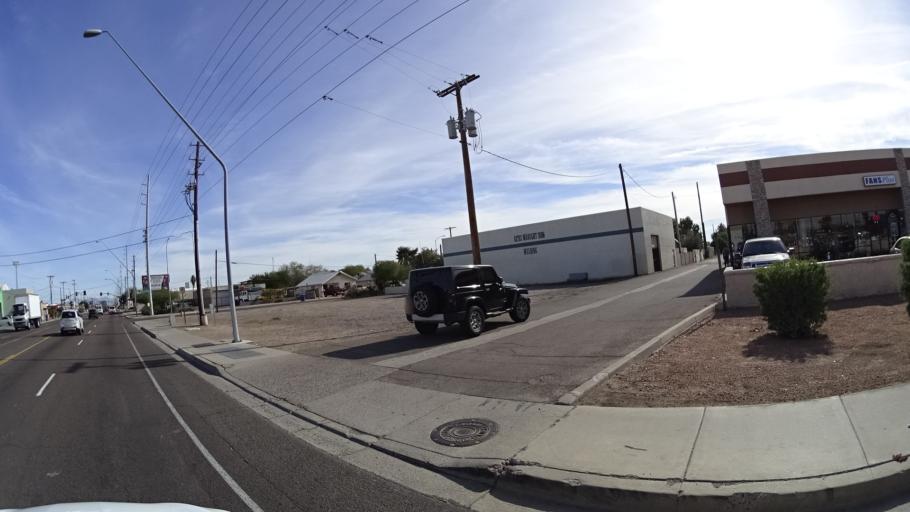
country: US
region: Arizona
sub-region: Maricopa County
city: Mesa
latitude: 33.4077
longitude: -111.8359
